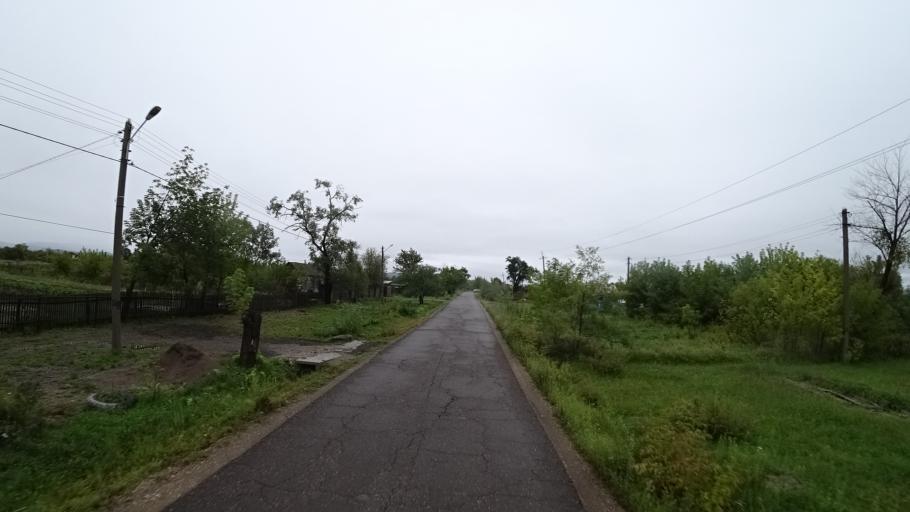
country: RU
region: Primorskiy
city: Monastyrishche
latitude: 44.2012
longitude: 132.4631
